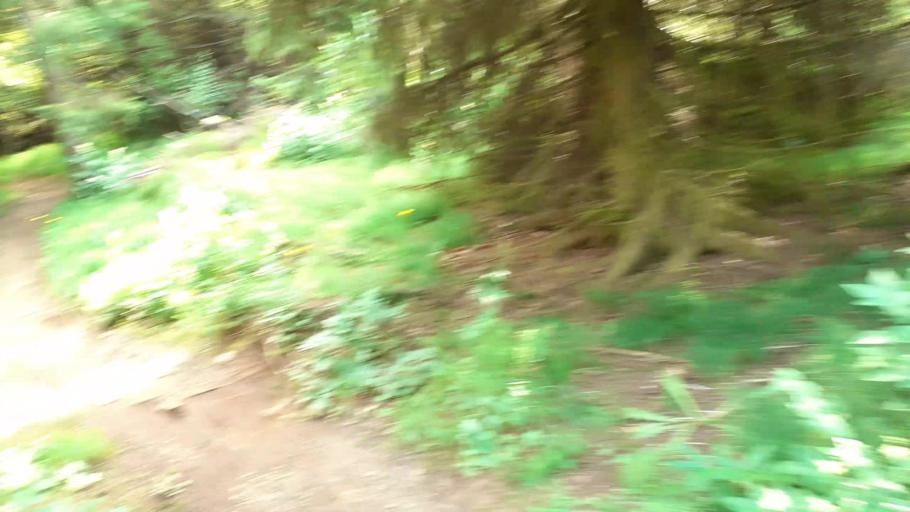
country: IS
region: Northeast
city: Akureyri
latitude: 65.6421
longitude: -18.0855
